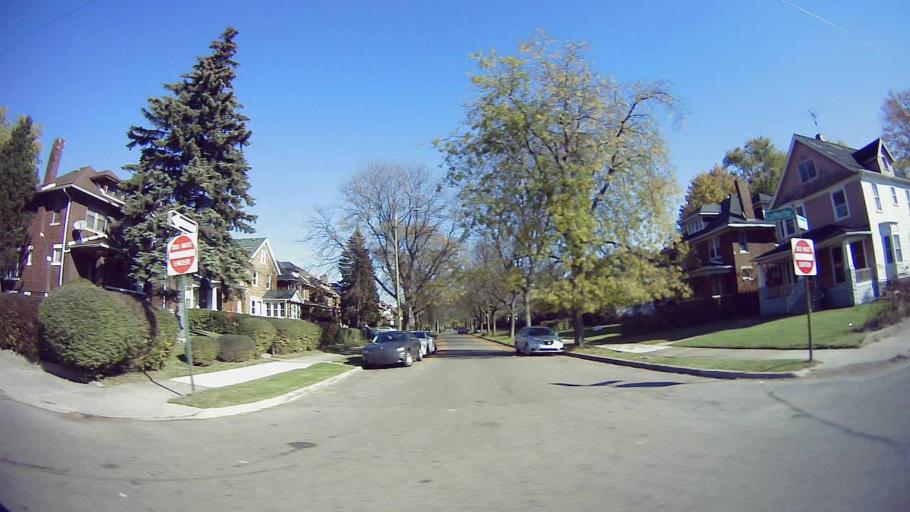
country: US
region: Michigan
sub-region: Wayne County
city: Highland Park
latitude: 42.3628
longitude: -83.1016
